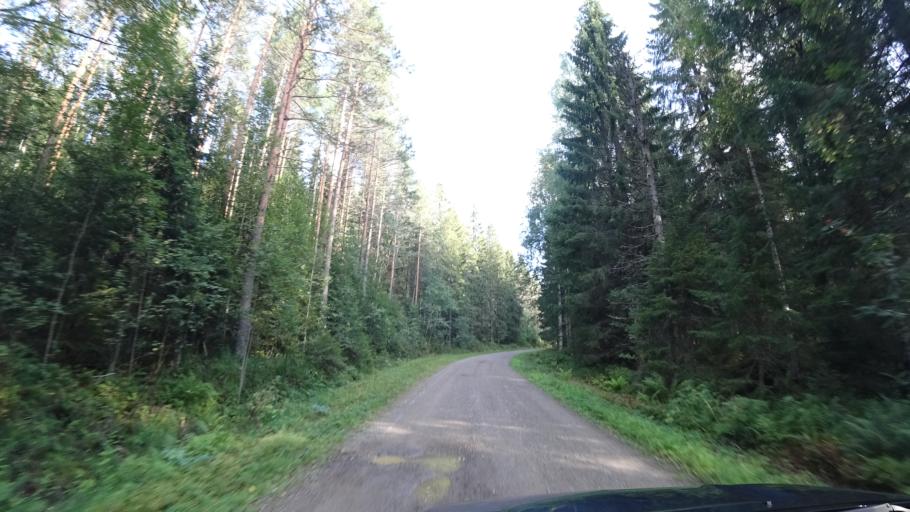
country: FI
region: Paijanne Tavastia
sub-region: Lahti
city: Auttoinen
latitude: 61.2191
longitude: 25.1498
